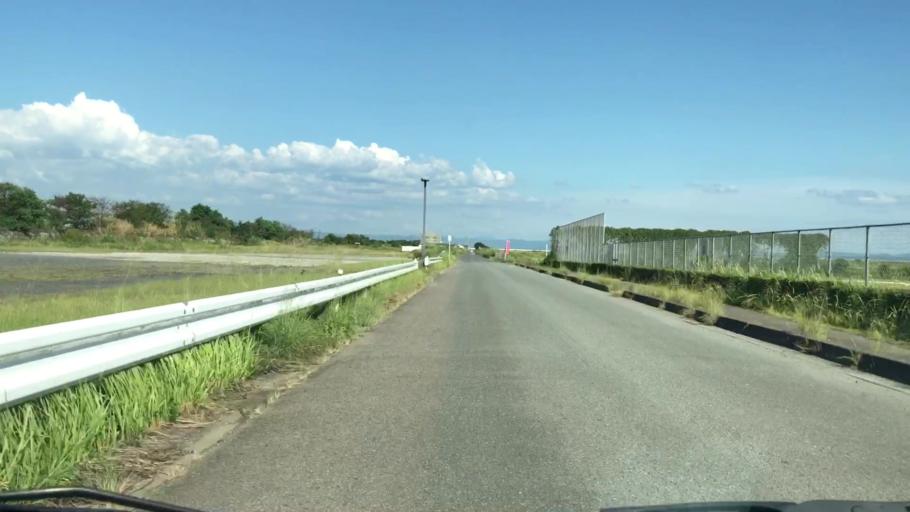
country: JP
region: Saga Prefecture
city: Okawa
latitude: 33.1520
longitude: 130.3124
